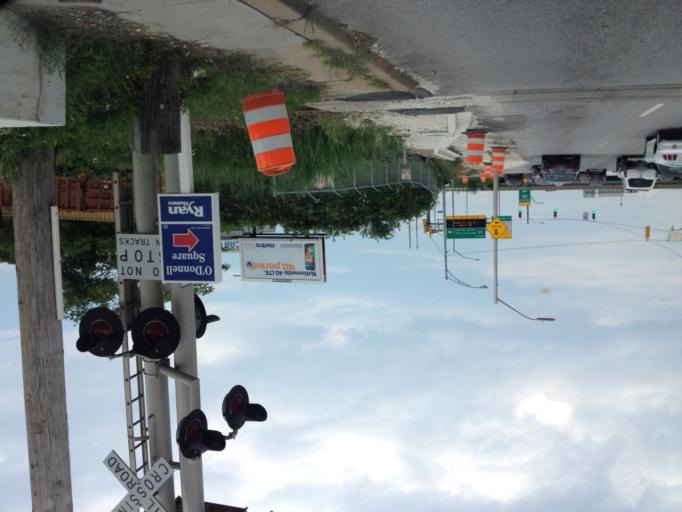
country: US
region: Maryland
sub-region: Baltimore County
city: Dundalk
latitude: 39.2808
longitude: -76.5556
